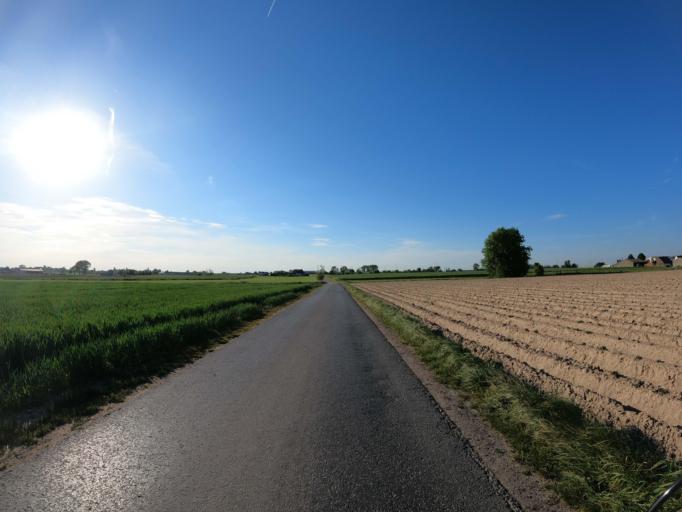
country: BE
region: Flanders
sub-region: Provincie West-Vlaanderen
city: Dentergem
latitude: 50.9954
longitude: 3.4525
